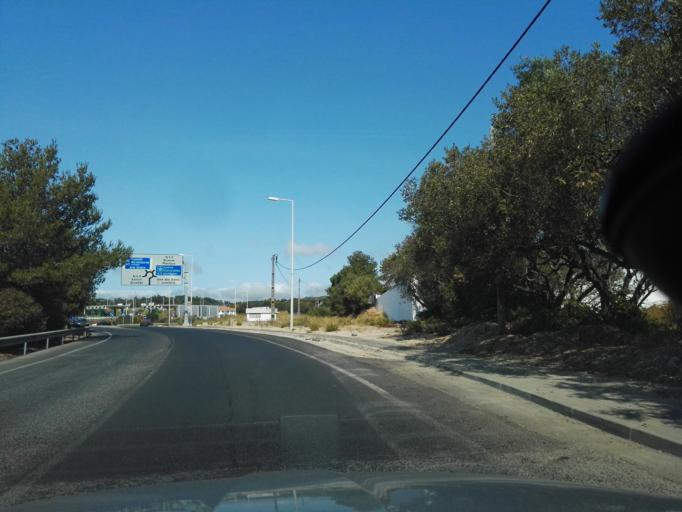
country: PT
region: Lisbon
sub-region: Cascais
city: Estoril
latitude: 38.7141
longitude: -9.3874
